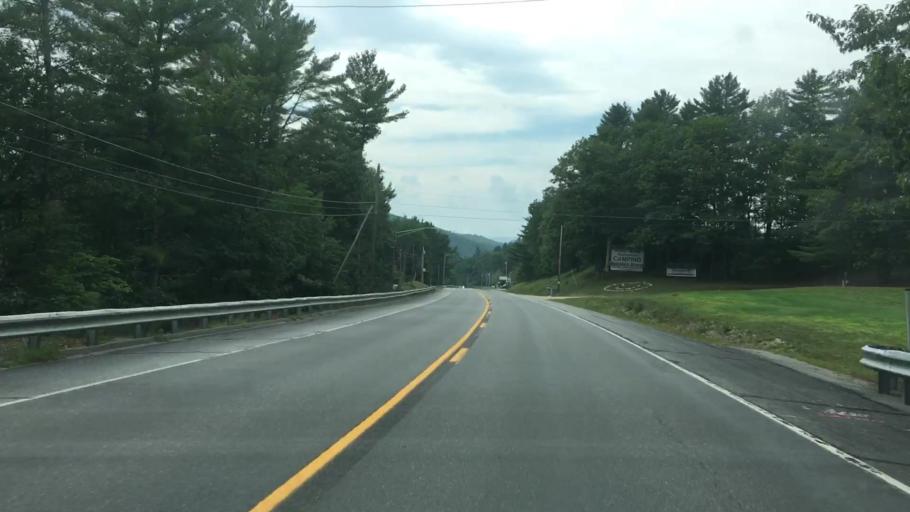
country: US
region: Maine
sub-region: Oxford County
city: Bethel
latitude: 44.4883
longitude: -70.7717
